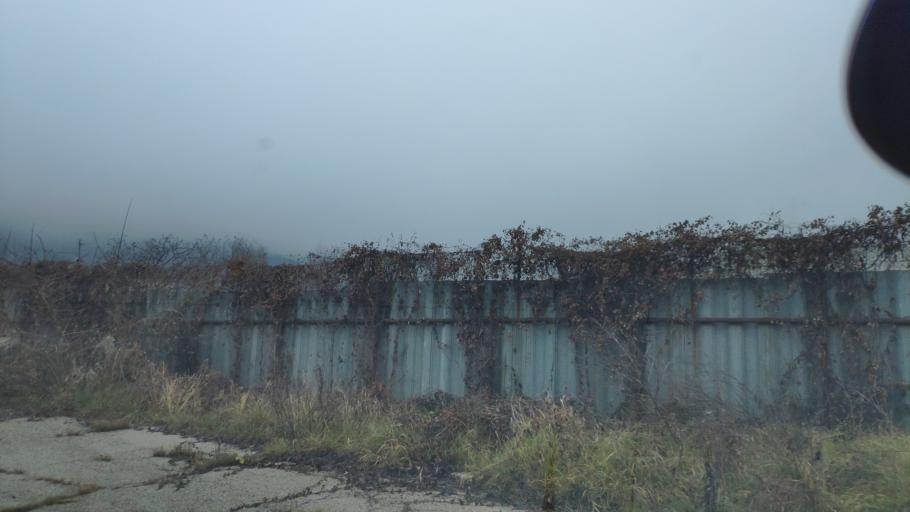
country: SK
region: Banskobystricky
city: Revuca
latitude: 48.6291
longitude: 20.2423
